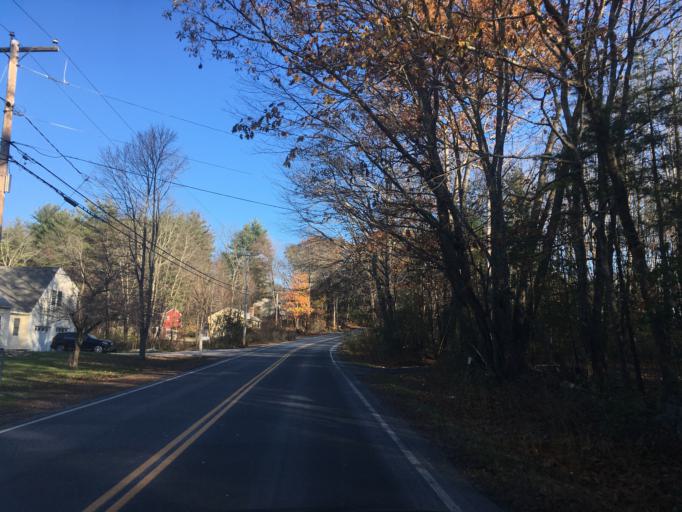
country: US
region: New Hampshire
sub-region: Rockingham County
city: Stratham Station
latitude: 43.0389
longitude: -70.9076
